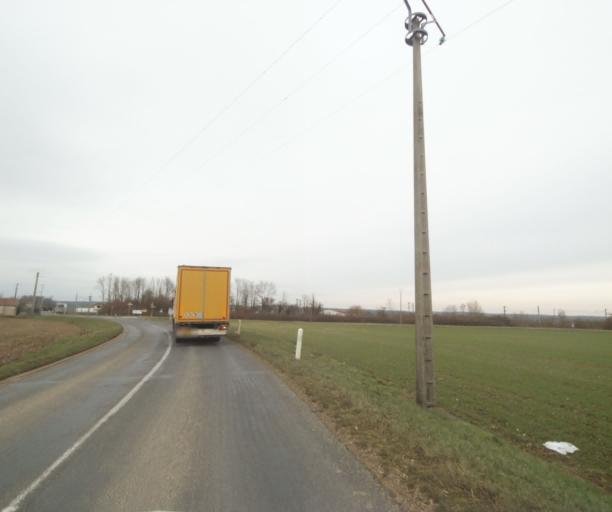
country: FR
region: Champagne-Ardenne
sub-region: Departement de la Haute-Marne
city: Villiers-en-Lieu
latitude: 48.6556
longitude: 4.9093
